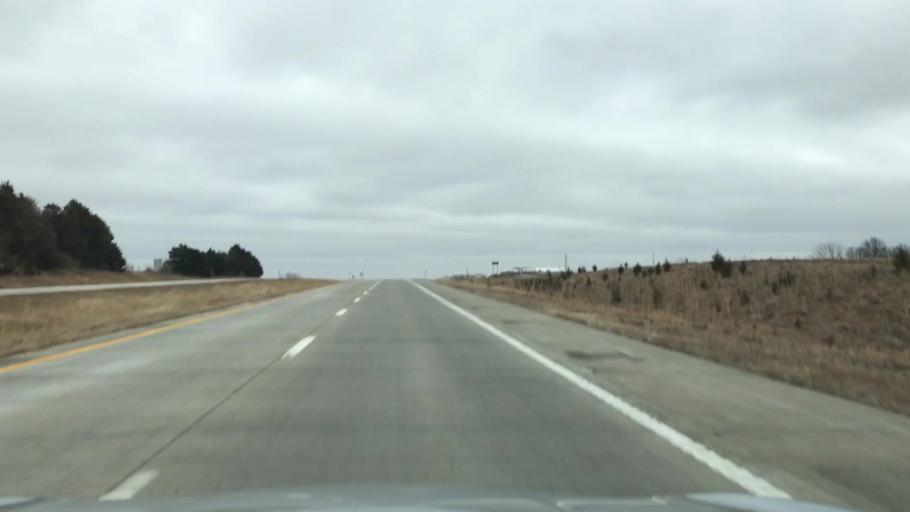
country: US
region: Missouri
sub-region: Caldwell County
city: Hamilton
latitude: 39.7351
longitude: -93.8563
